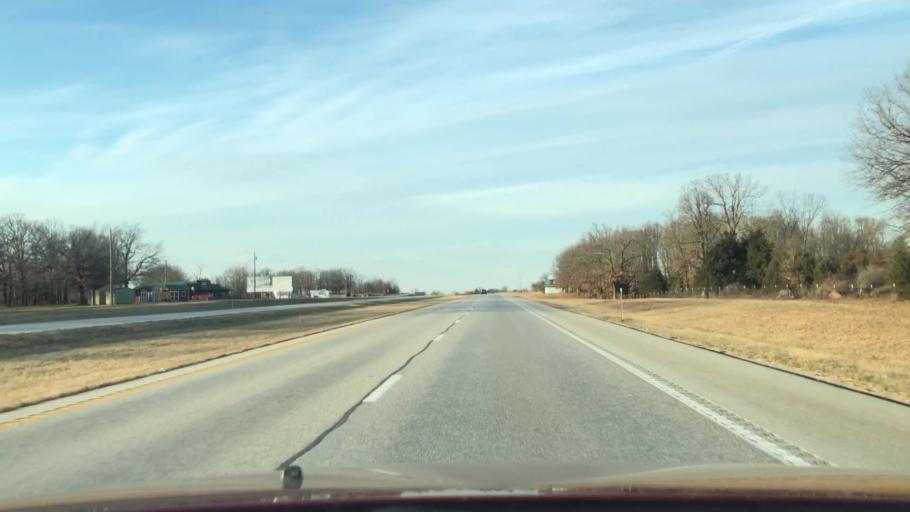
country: US
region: Missouri
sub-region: Webster County
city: Seymour
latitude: 37.1404
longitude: -92.7455
